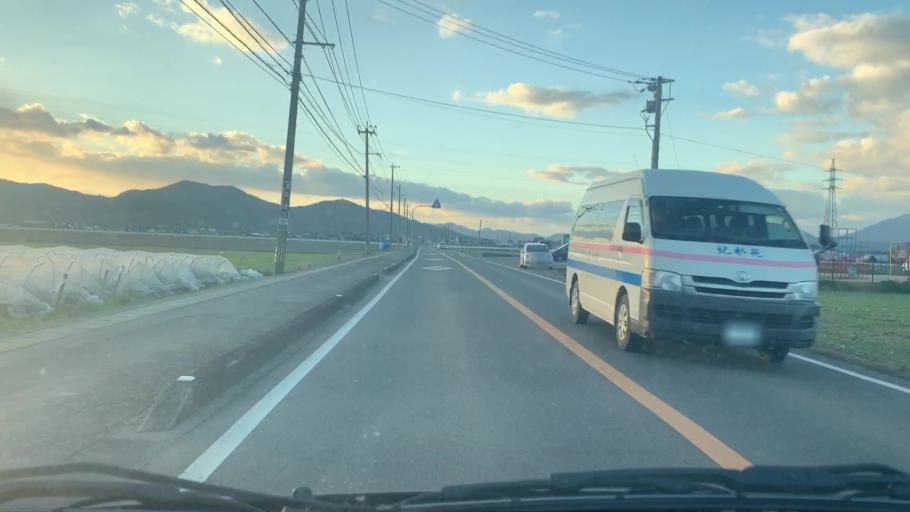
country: JP
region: Saga Prefecture
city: Kashima
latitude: 33.1910
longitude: 130.1299
